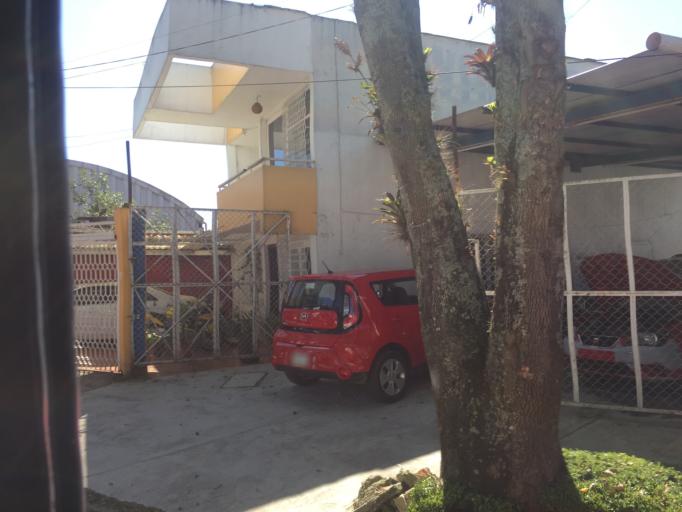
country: MX
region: Veracruz
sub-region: Xalapa
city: Xalapa de Enriquez
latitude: 19.5432
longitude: -96.9265
